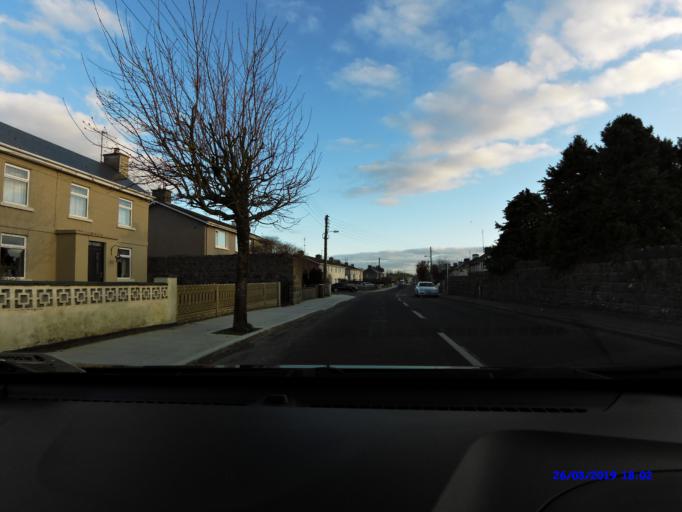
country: IE
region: Connaught
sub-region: County Galway
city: Tuam
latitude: 53.5088
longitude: -8.8442
